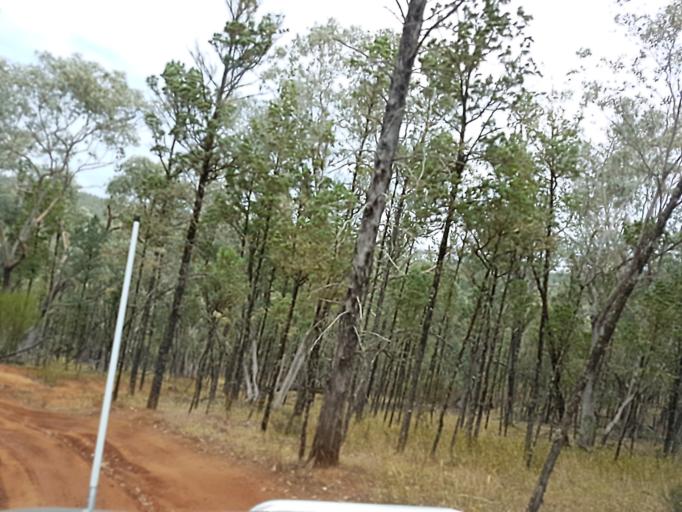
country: AU
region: New South Wales
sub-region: Snowy River
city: Jindabyne
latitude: -36.9294
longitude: 148.3910
